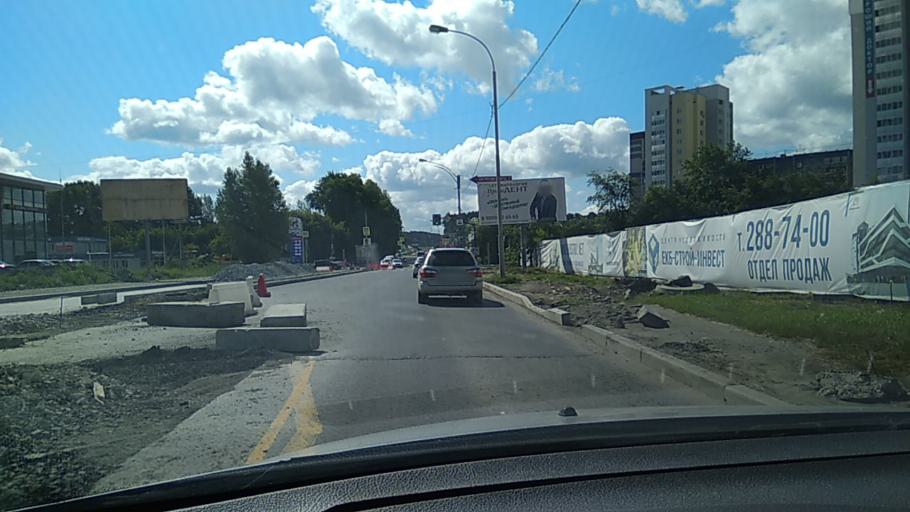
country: RU
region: Sverdlovsk
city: Yekaterinburg
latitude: 56.7993
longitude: 60.5948
